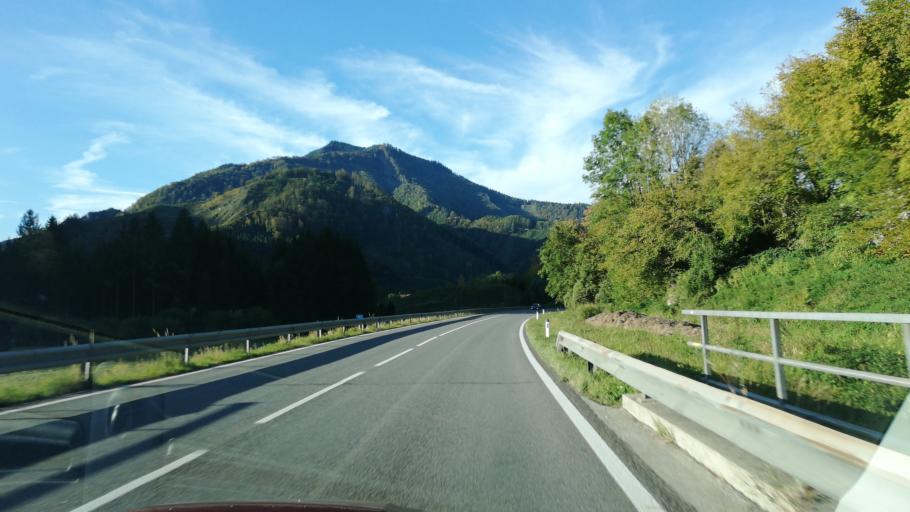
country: AT
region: Styria
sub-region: Politischer Bezirk Liezen
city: Altenmarkt bei Sankt Gallen
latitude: 47.7460
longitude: 14.6436
